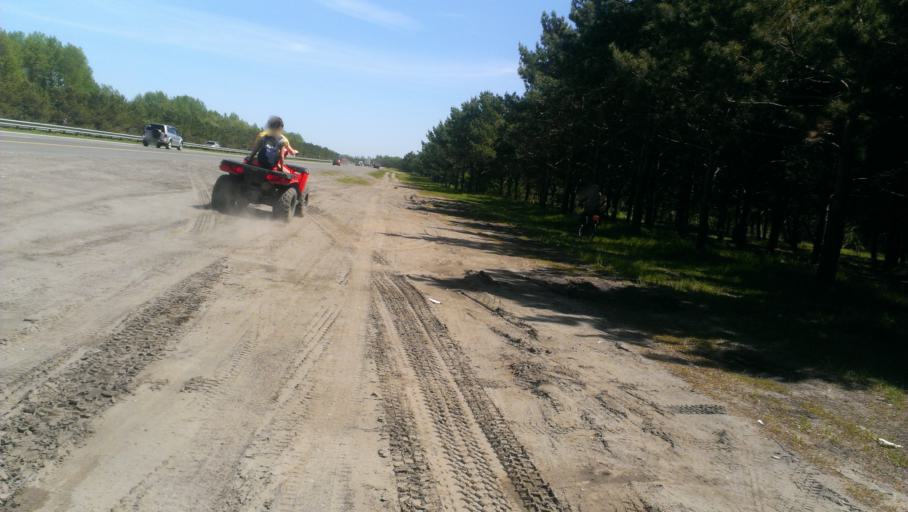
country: RU
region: Altai Krai
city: Zaton
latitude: 53.3150
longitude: 83.8451
